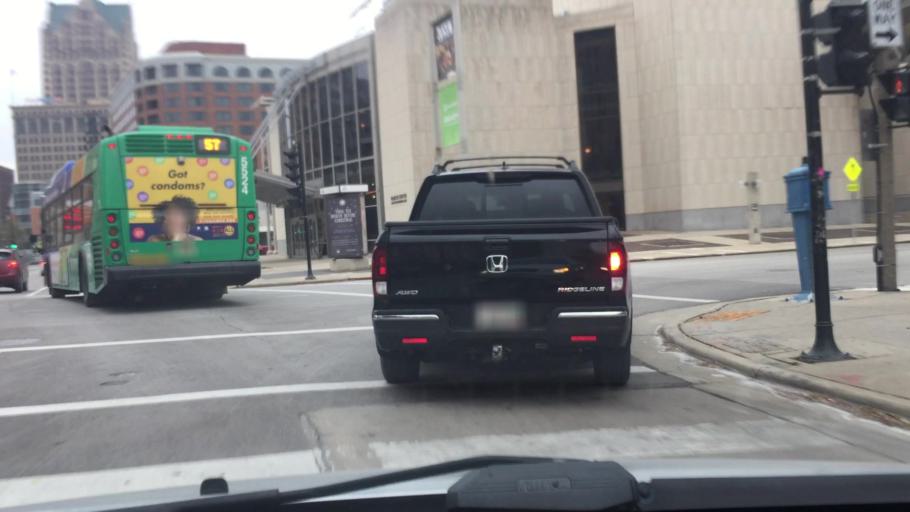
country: US
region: Wisconsin
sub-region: Milwaukee County
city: Milwaukee
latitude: 43.0435
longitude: -87.9110
